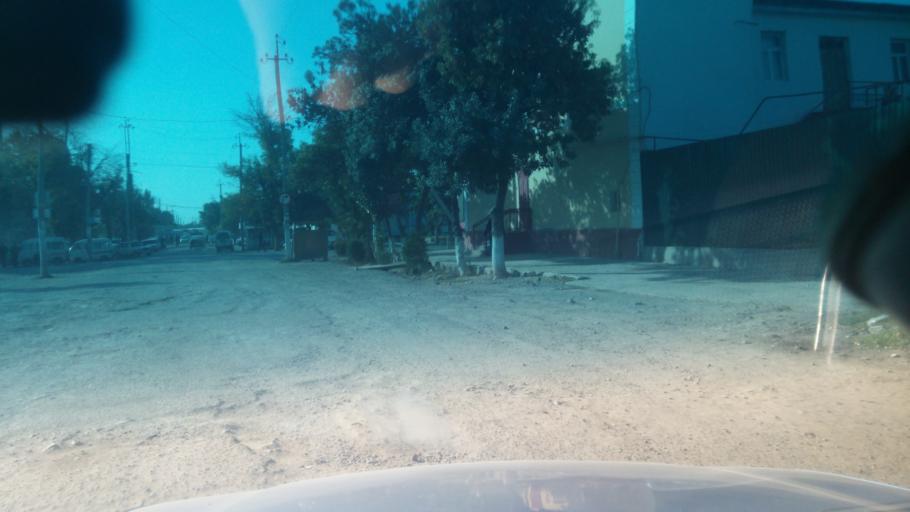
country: UZ
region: Sirdaryo
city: Guliston
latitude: 40.4966
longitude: 68.7690
